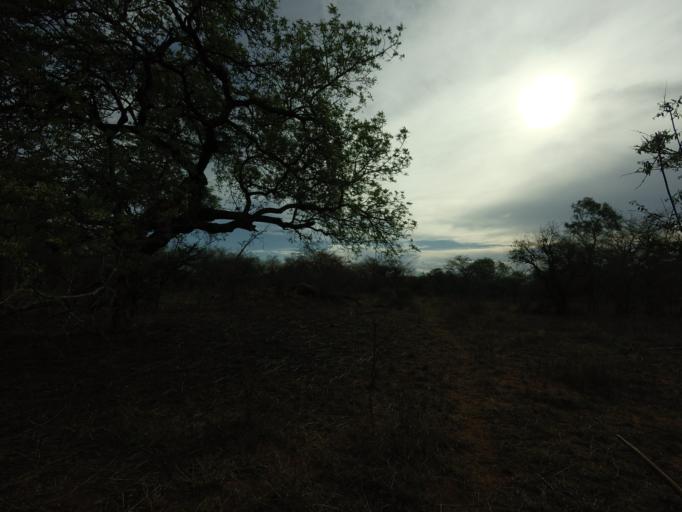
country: ZA
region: Limpopo
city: Thulamahashi
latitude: -24.5286
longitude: 31.1167
